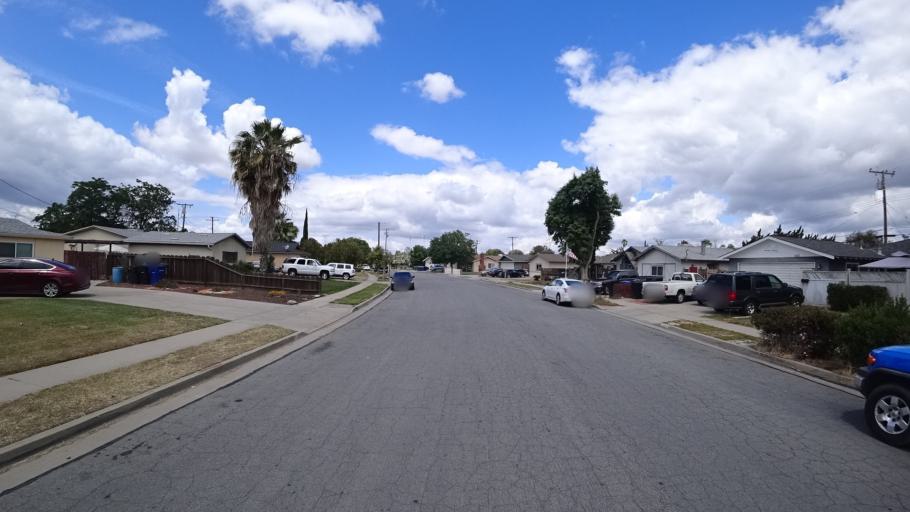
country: US
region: California
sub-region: Kings County
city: Hanford
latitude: 36.3387
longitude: -119.6269
